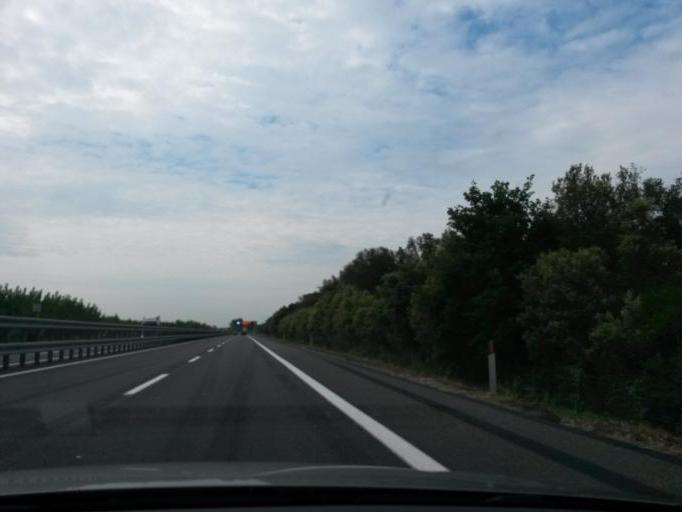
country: IT
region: Tuscany
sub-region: Province of Pisa
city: Migliarino
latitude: 43.7988
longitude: 10.3187
